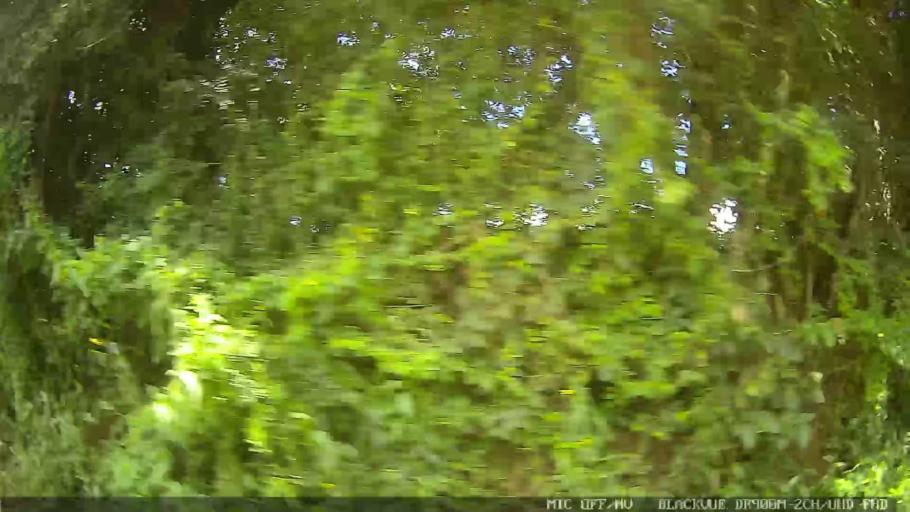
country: BR
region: Sao Paulo
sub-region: Amparo
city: Amparo
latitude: -22.8613
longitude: -46.7595
